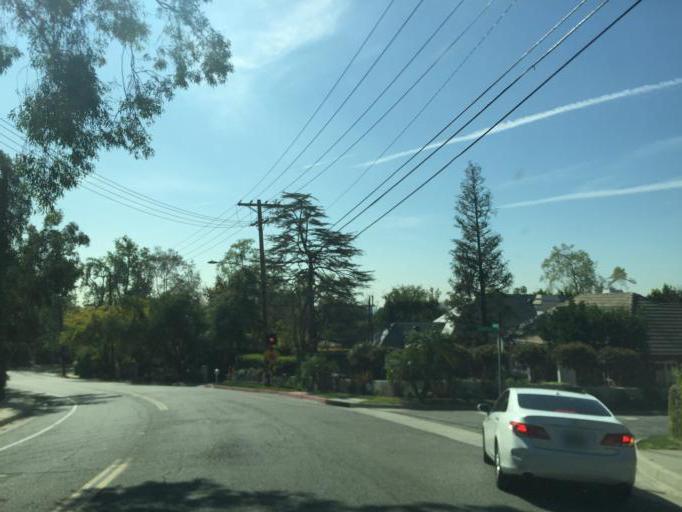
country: US
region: California
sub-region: Los Angeles County
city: South Pasadena
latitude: 34.1192
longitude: -118.1319
